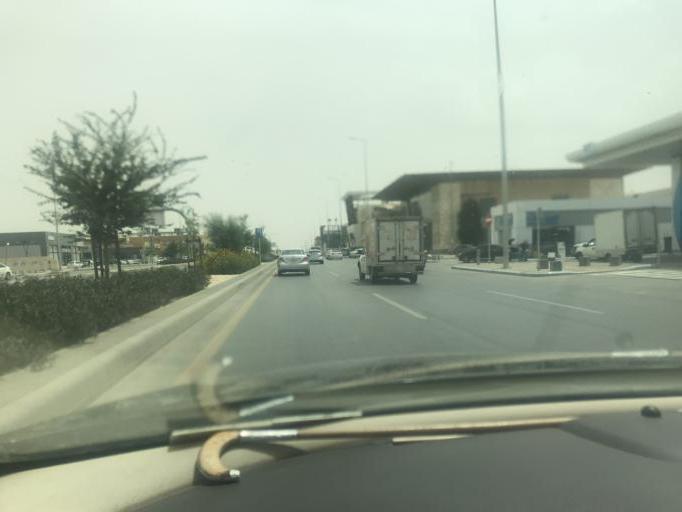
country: SA
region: Ar Riyad
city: Riyadh
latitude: 24.7365
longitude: 46.7821
